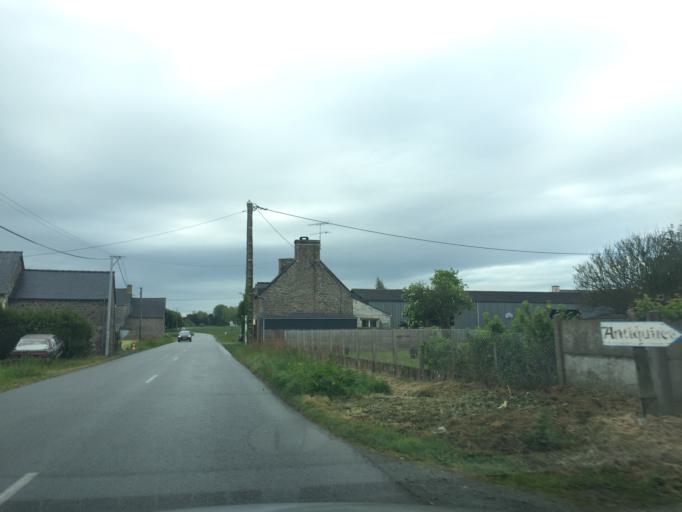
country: FR
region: Brittany
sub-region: Departement des Cotes-d'Armor
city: Crehen
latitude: 48.5599
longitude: -2.2406
